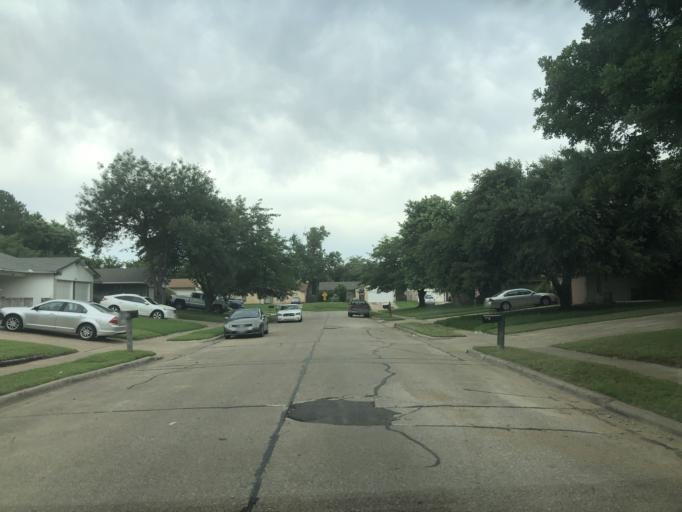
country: US
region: Texas
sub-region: Dallas County
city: Irving
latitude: 32.7844
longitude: -96.9642
